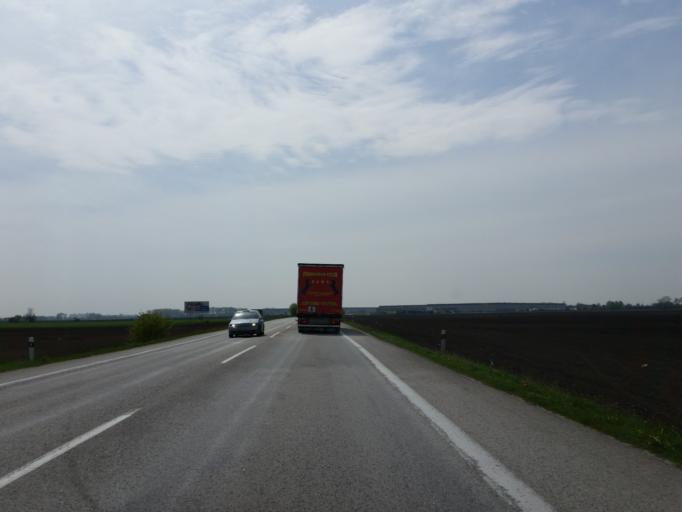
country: SK
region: Trnavsky
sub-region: Okres Galanta
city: Galanta
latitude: 48.2452
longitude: 17.7371
